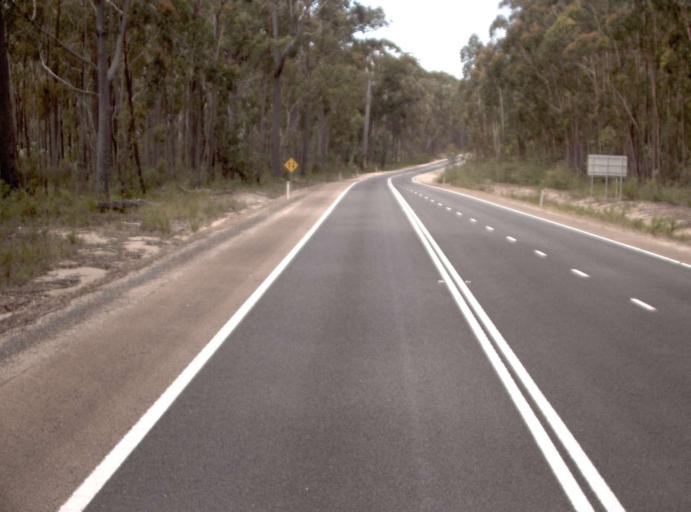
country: AU
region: New South Wales
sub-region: Bega Valley
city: Eden
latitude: -37.5024
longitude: 149.5365
